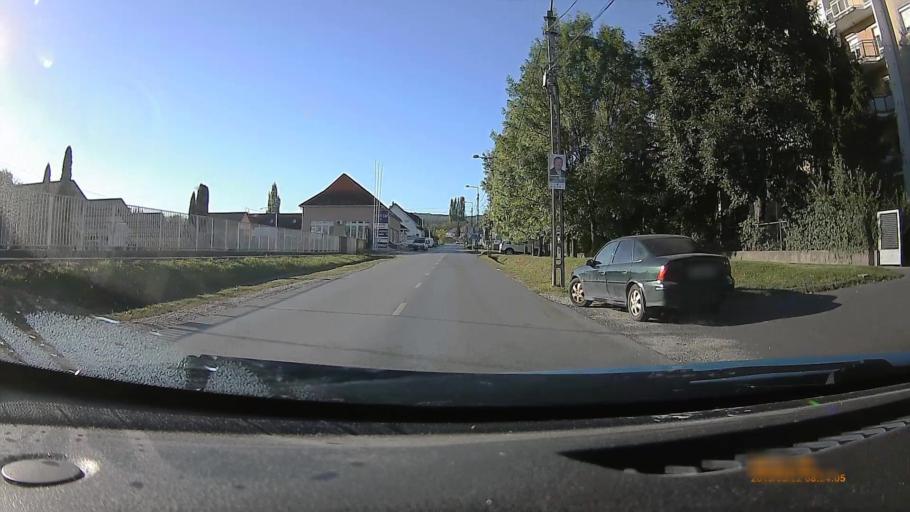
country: HU
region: Borsod-Abauj-Zemplen
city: Miskolc
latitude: 48.0932
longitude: 20.7112
